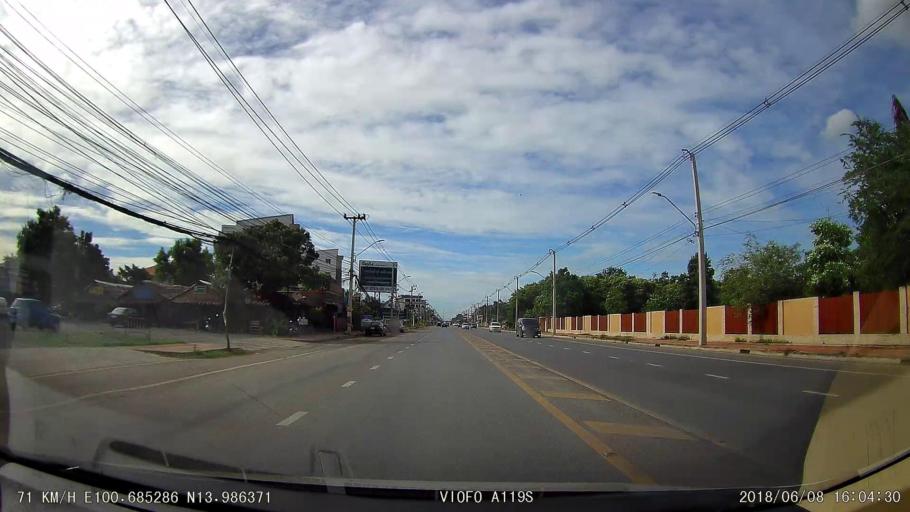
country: TH
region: Pathum Thani
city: Thanyaburi
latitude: 13.9866
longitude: 100.6853
